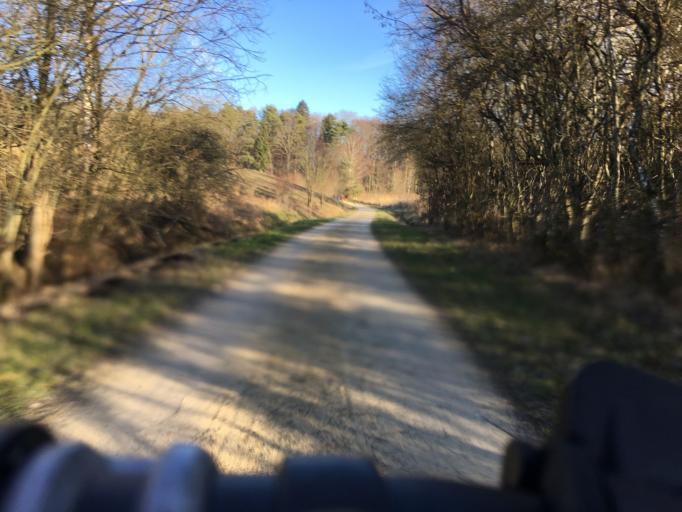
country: DE
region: Baden-Wuerttemberg
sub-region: Freiburg Region
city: Moos
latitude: 47.7201
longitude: 8.9199
